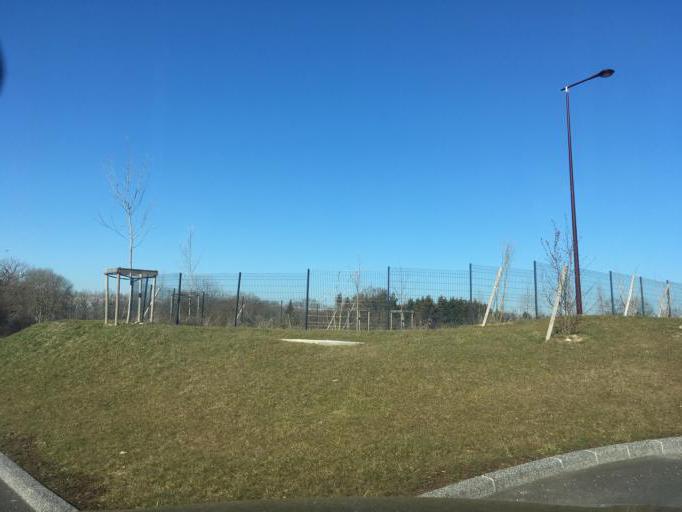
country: FR
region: Rhone-Alpes
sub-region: Departement de la Haute-Savoie
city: Cranves-Sales
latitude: 46.1879
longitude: 6.2847
